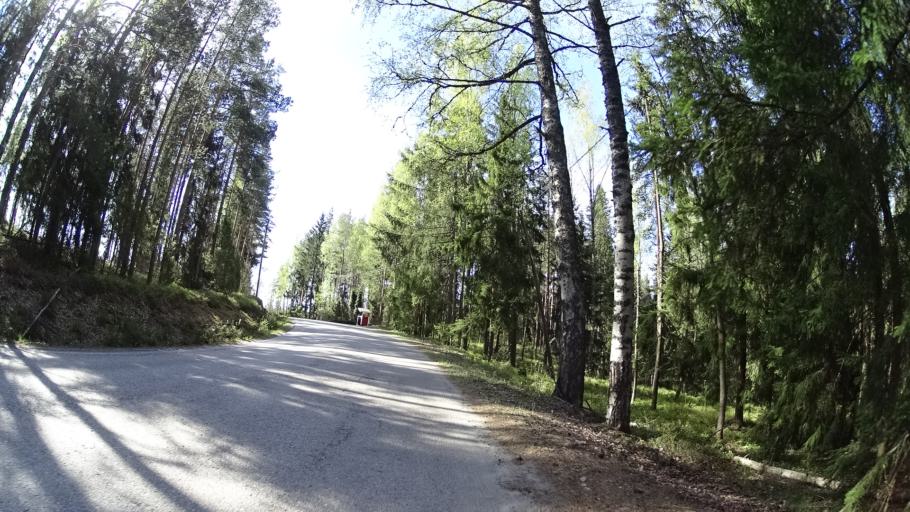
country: FI
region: Uusimaa
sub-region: Helsinki
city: Nurmijaervi
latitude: 60.4493
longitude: 24.8245
